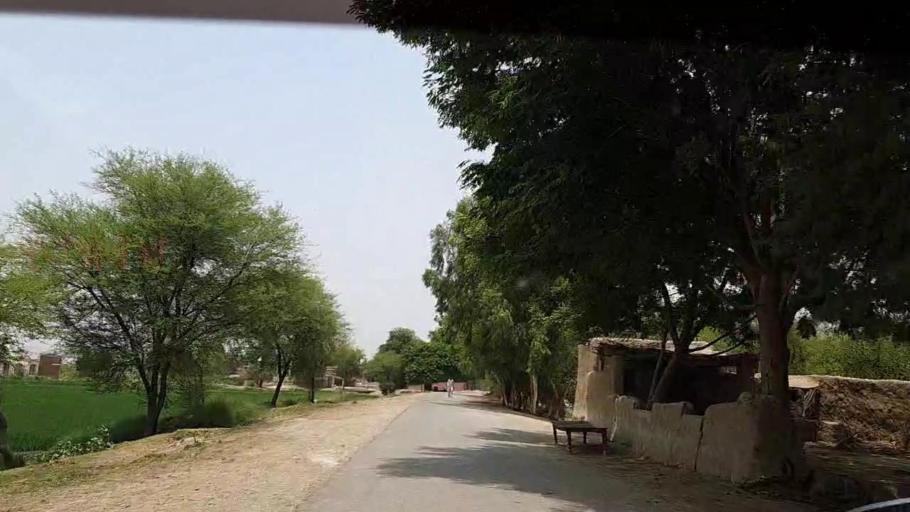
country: PK
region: Sindh
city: Khairpur Nathan Shah
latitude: 27.0165
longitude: 67.6697
